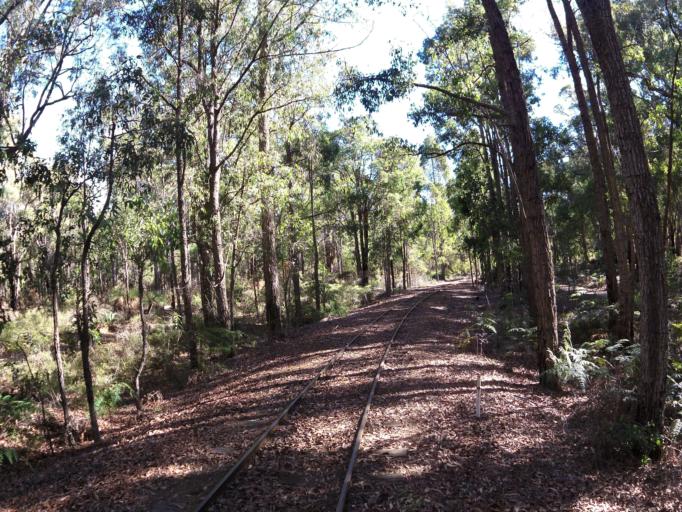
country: AU
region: Western Australia
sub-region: Waroona
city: Waroona
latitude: -32.7117
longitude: 116.0759
